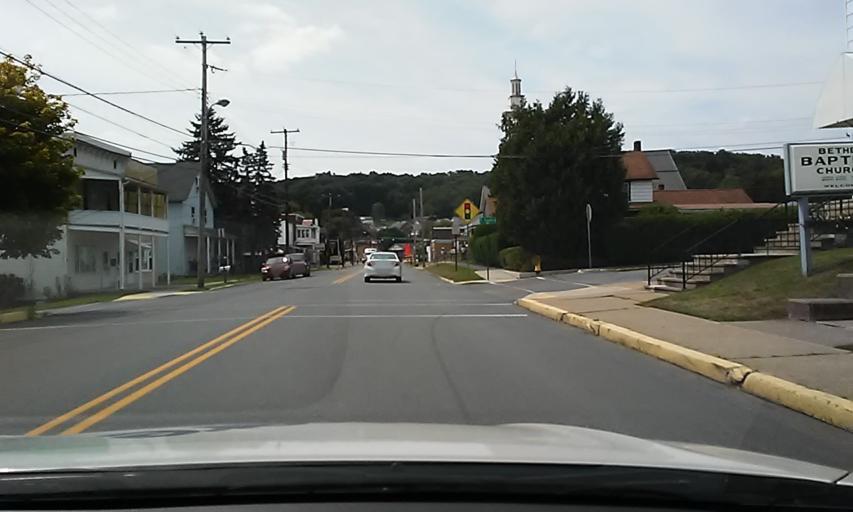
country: US
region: Pennsylvania
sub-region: Jefferson County
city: Sykesville
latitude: 41.0513
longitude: -78.8203
